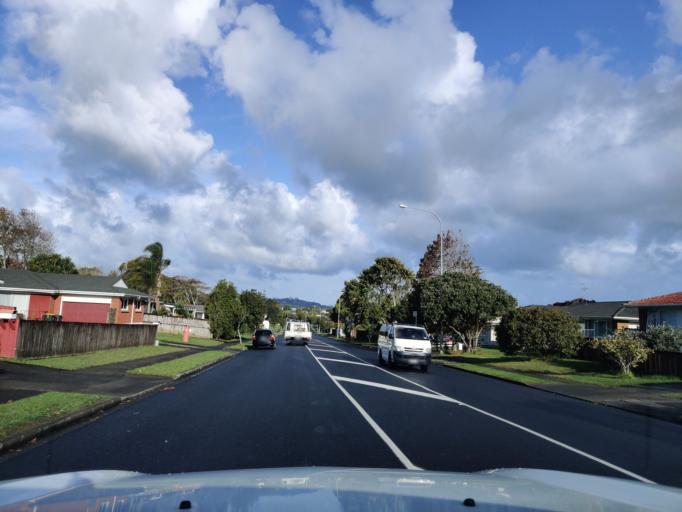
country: NZ
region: Auckland
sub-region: Auckland
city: Pakuranga
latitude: -36.9074
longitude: 174.8971
